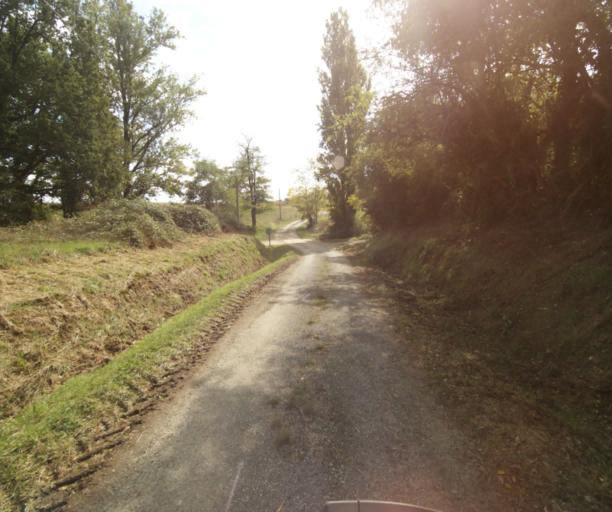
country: FR
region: Midi-Pyrenees
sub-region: Departement du Tarn-et-Garonne
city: Verdun-sur-Garonne
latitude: 43.8687
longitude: 1.1949
